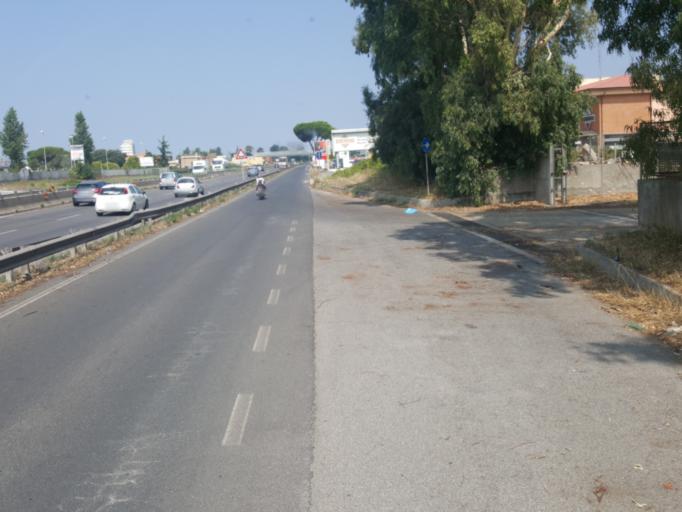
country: IT
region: Latium
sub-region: Provincia di Latina
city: Aprilia
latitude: 41.5748
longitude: 12.6593
